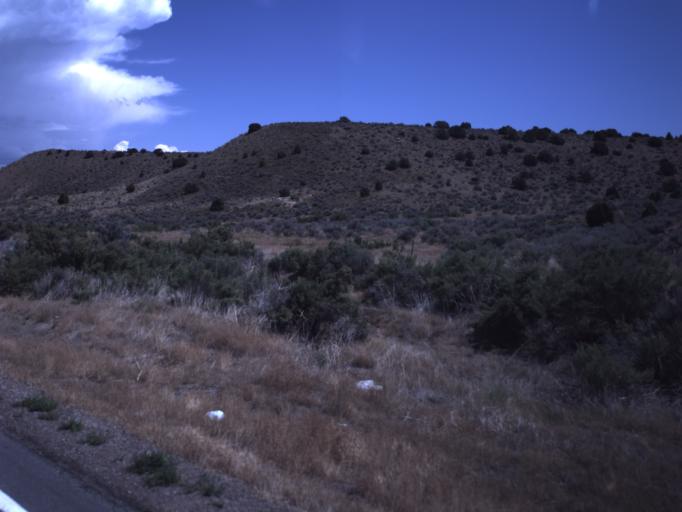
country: US
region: Utah
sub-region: Uintah County
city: Maeser
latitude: 40.4565
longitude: -109.6178
